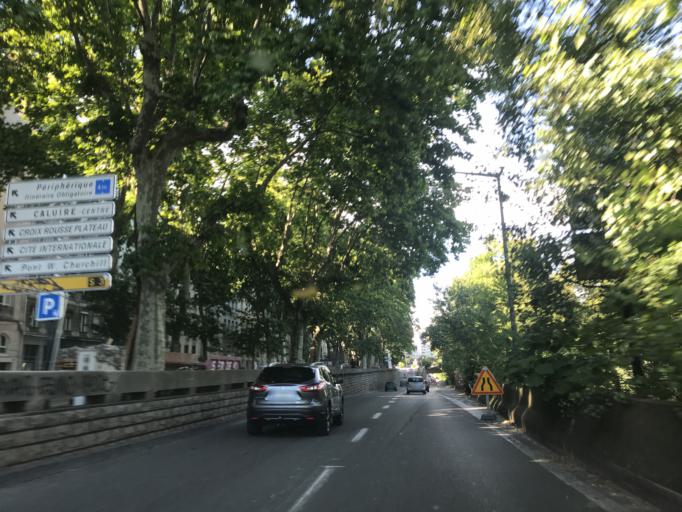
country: FR
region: Rhone-Alpes
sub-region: Departement du Rhone
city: Caluire-et-Cuire
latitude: 45.7767
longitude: 4.8401
